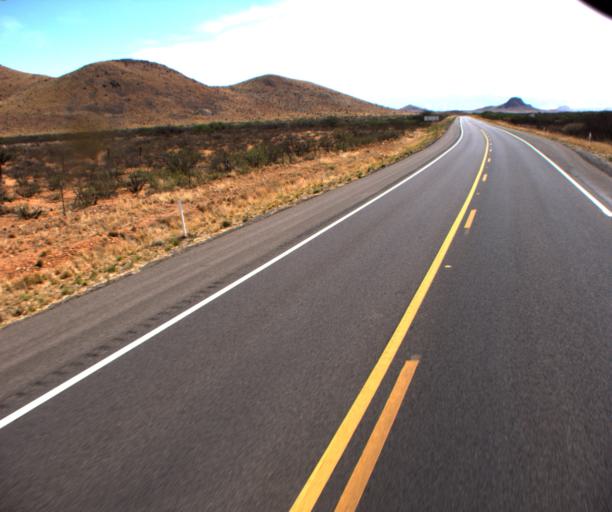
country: US
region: Arizona
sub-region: Cochise County
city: Tombstone
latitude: 31.9051
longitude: -109.8080
